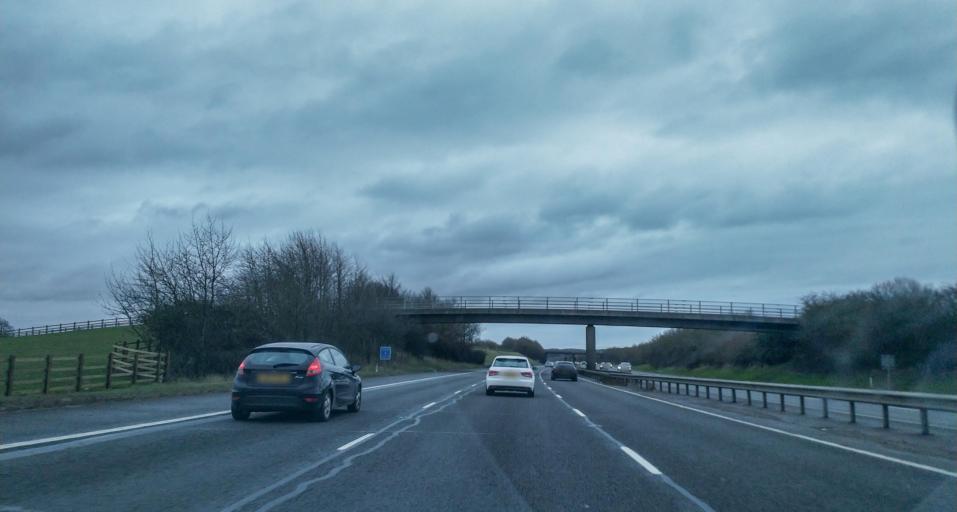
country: GB
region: England
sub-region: Warwickshire
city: Harbury
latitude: 52.2261
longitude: -1.5186
